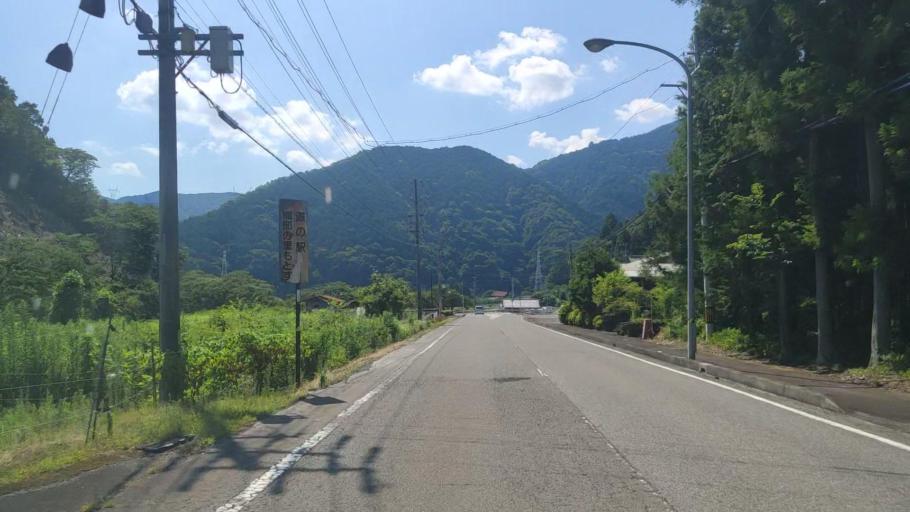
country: JP
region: Gifu
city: Godo
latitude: 35.5640
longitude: 136.6426
